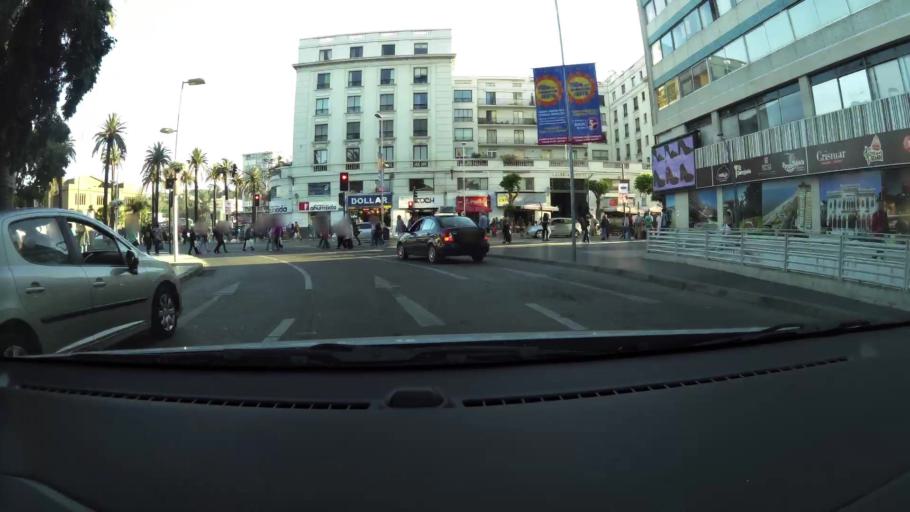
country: CL
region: Valparaiso
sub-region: Provincia de Valparaiso
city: Vina del Mar
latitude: -33.0246
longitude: -71.5527
